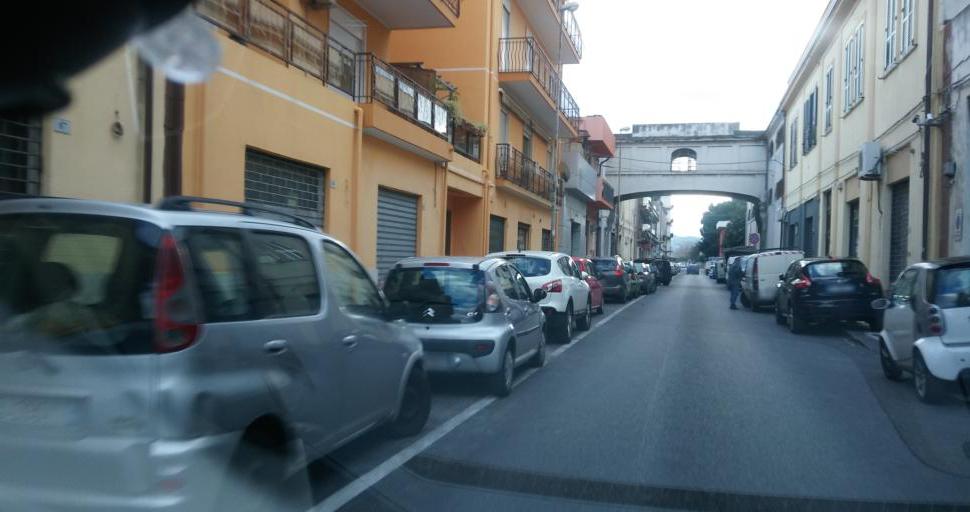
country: IT
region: Sicily
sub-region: Messina
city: Milazzo
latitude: 38.2139
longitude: 15.2434
